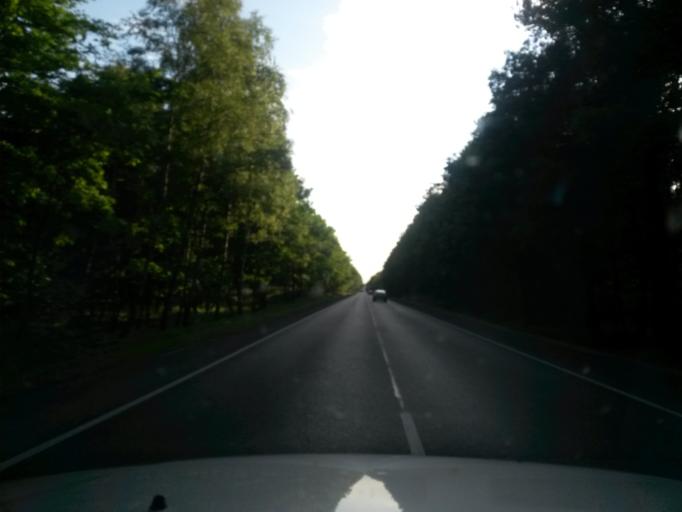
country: PL
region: Lodz Voivodeship
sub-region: Powiat belchatowski
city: Szczercow
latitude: 51.3357
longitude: 19.1687
